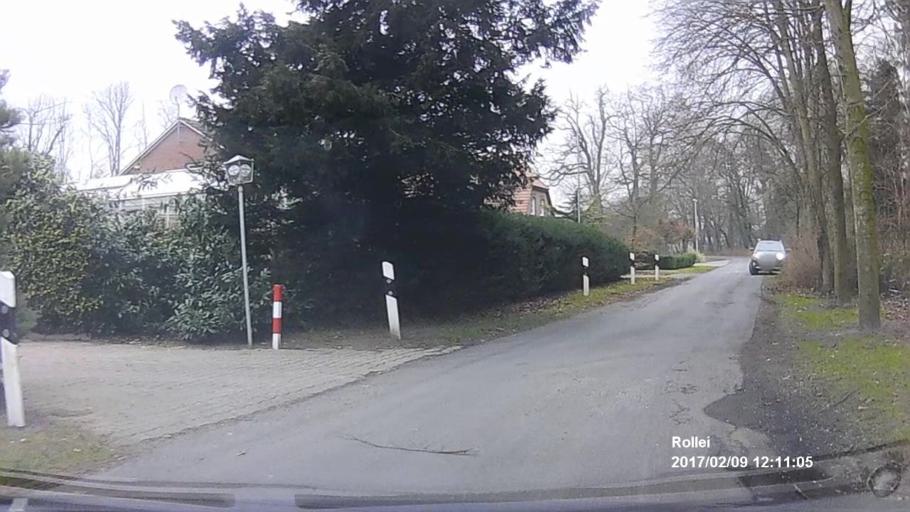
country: DE
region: Lower Saxony
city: Papenburg
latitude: 53.1065
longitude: 7.3605
